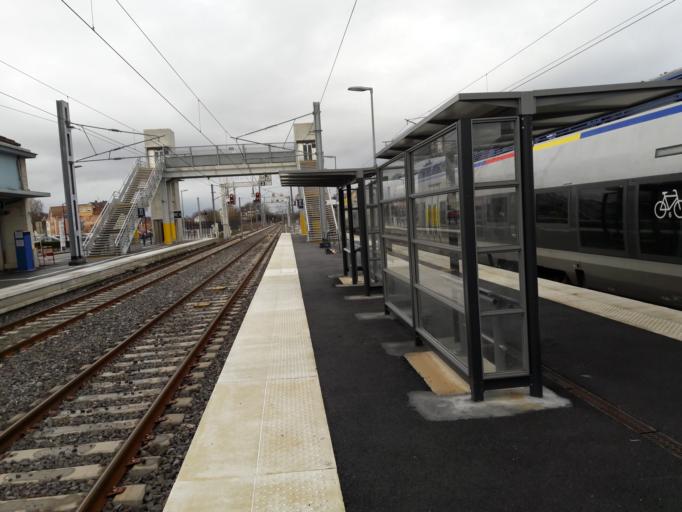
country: CH
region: Jura
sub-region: Porrentruy District
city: Boncourt
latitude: 47.5055
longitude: 7.0103
